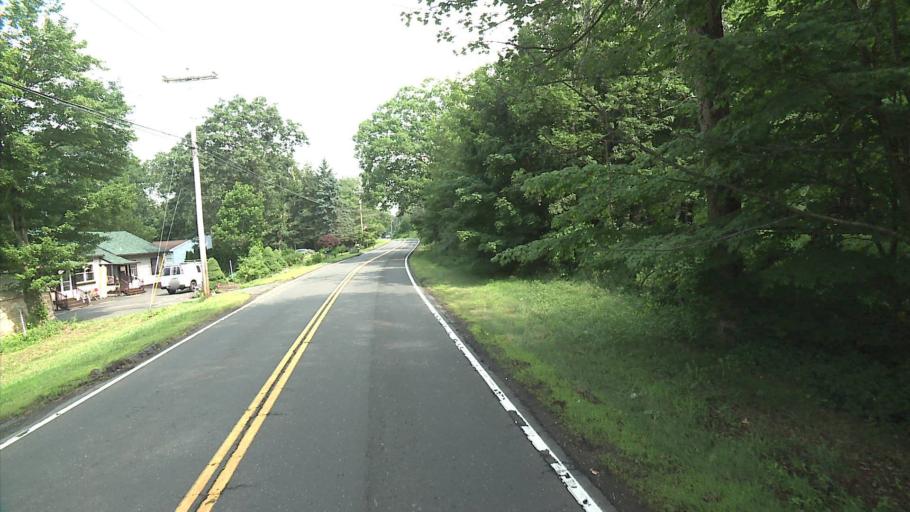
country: US
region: Connecticut
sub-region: New Haven County
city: Wolcott
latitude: 41.5911
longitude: -72.9568
